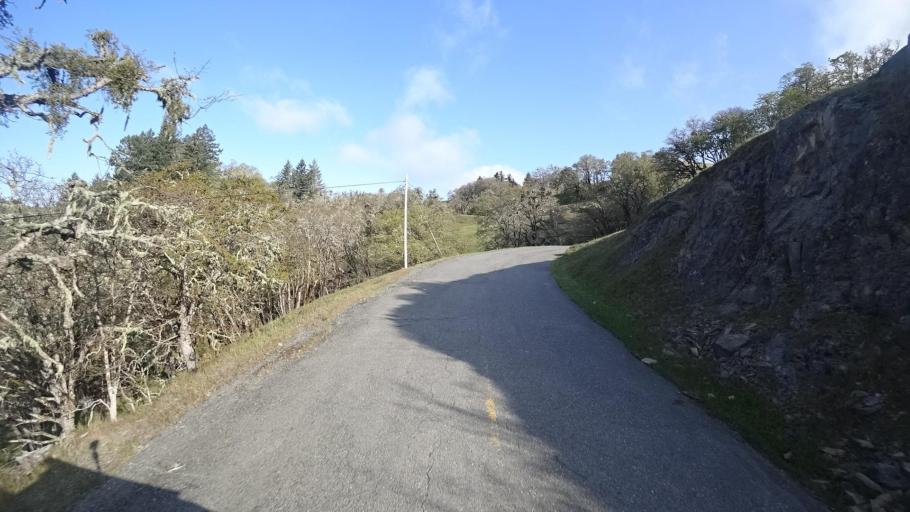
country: US
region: California
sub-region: Humboldt County
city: Blue Lake
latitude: 40.7149
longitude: -123.9376
